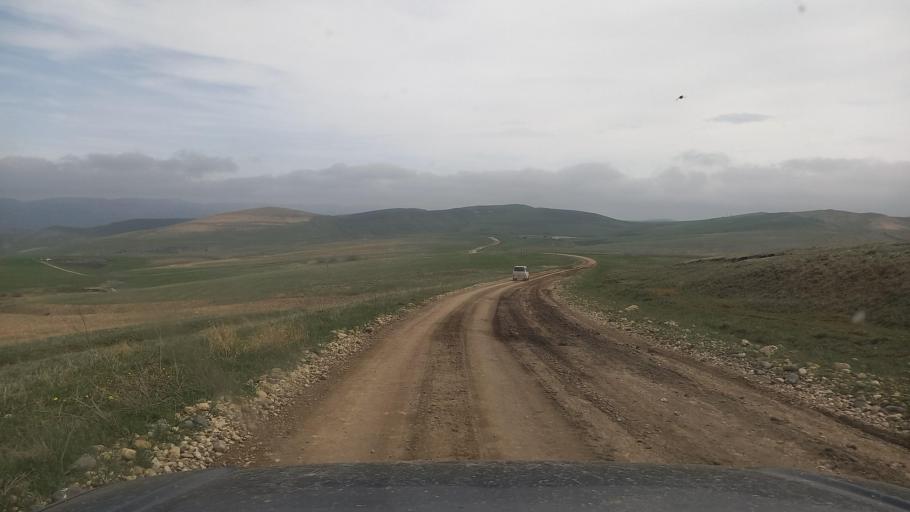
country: RU
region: Stavropol'skiy
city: Kislovodsk
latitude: 43.7691
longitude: 42.8346
